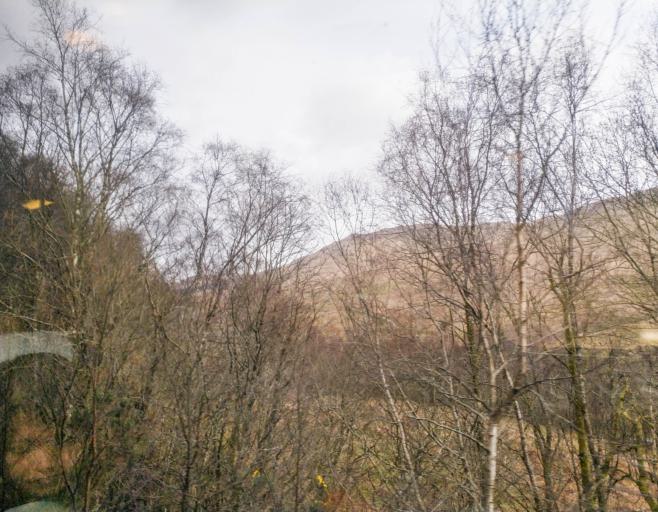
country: GB
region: Scotland
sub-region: Argyll and Bute
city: Garelochhead
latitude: 56.3561
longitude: -4.6852
